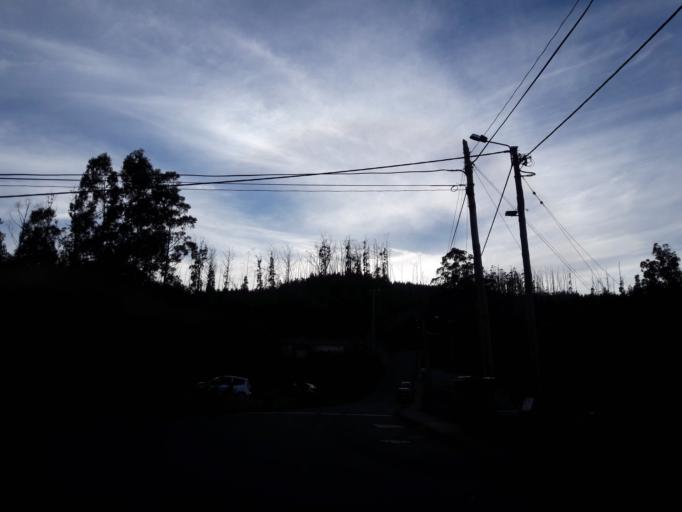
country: PT
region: Madeira
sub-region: Santa Cruz
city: Camacha
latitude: 32.6868
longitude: -16.8601
